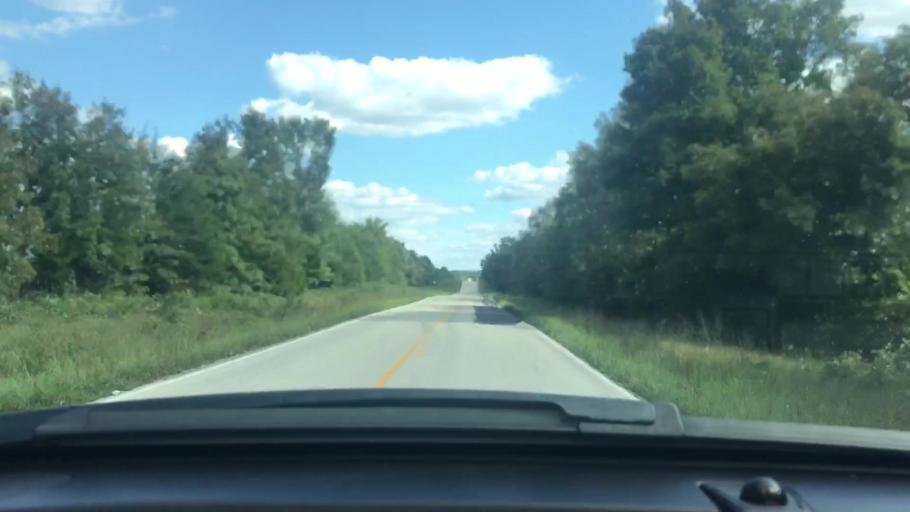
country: US
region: Missouri
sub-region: Wright County
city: Hartville
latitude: 37.3917
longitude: -92.4498
